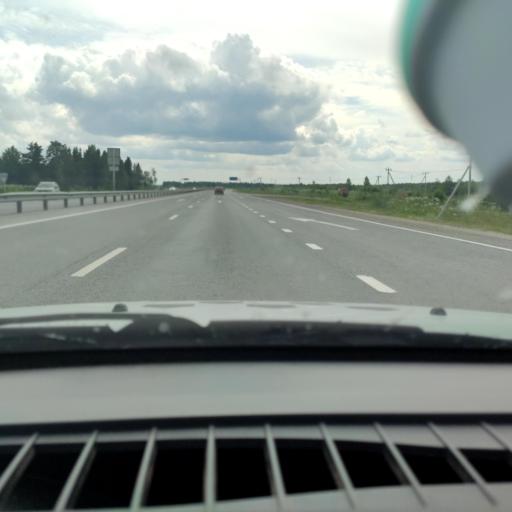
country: RU
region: Perm
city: Polazna
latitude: 58.2183
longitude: 56.4128
